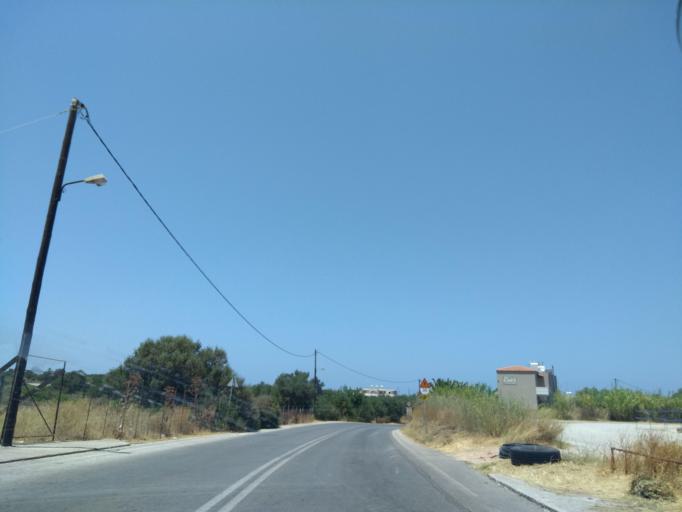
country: GR
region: Crete
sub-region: Nomos Chanias
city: Pithari
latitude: 35.5402
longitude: 24.0818
